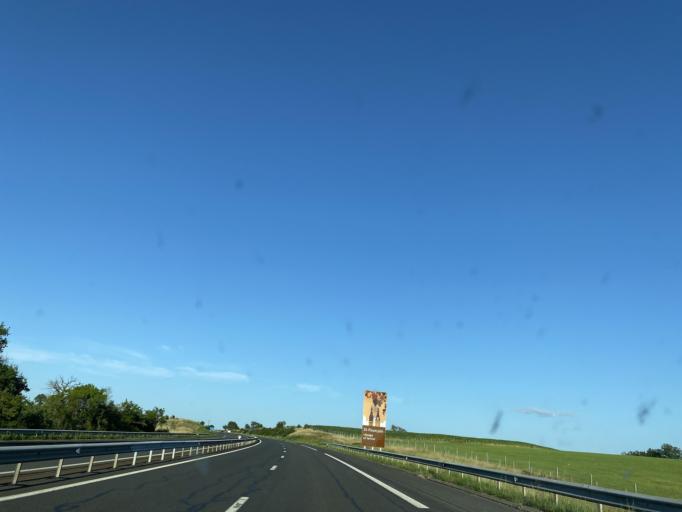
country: FR
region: Auvergne
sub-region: Departement de l'Allier
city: Doyet
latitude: 46.3545
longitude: 2.7656
